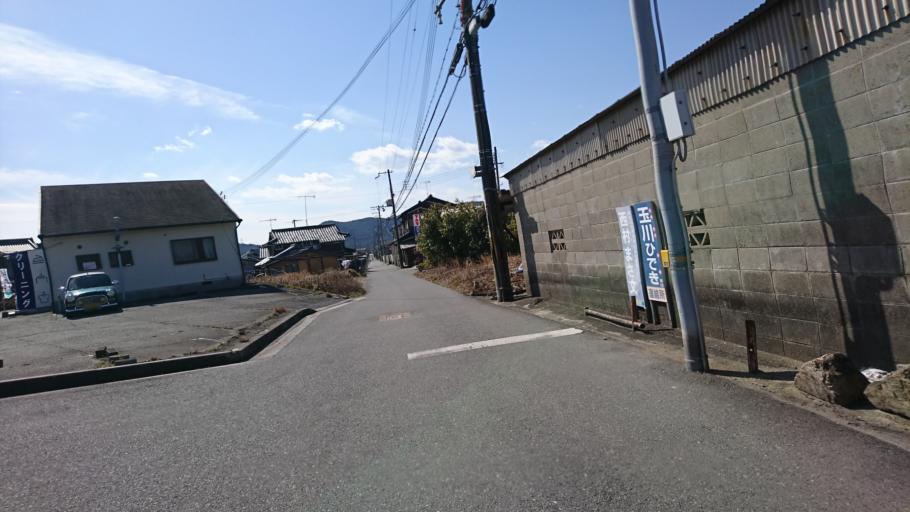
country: JP
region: Hyogo
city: Kakogawacho-honmachi
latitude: 34.8143
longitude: 134.8183
